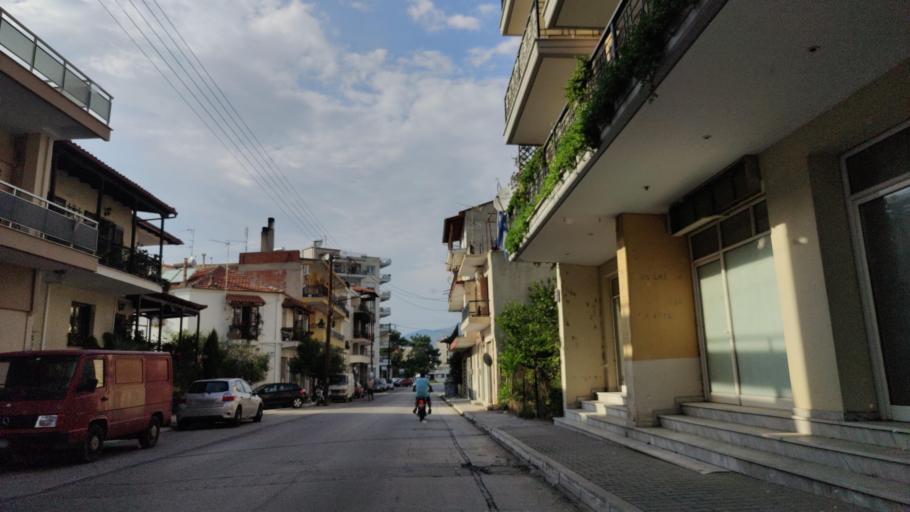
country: GR
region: Central Macedonia
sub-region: Nomos Serron
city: Sidirokastro
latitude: 41.2333
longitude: 23.3902
